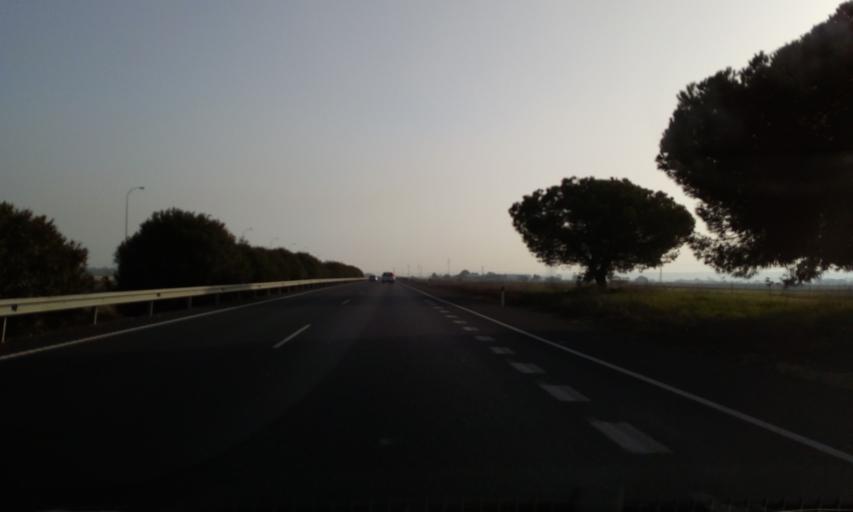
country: ES
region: Andalusia
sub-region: Provincia de Huelva
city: San Juan del Puerto
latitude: 37.3329
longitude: -6.7962
